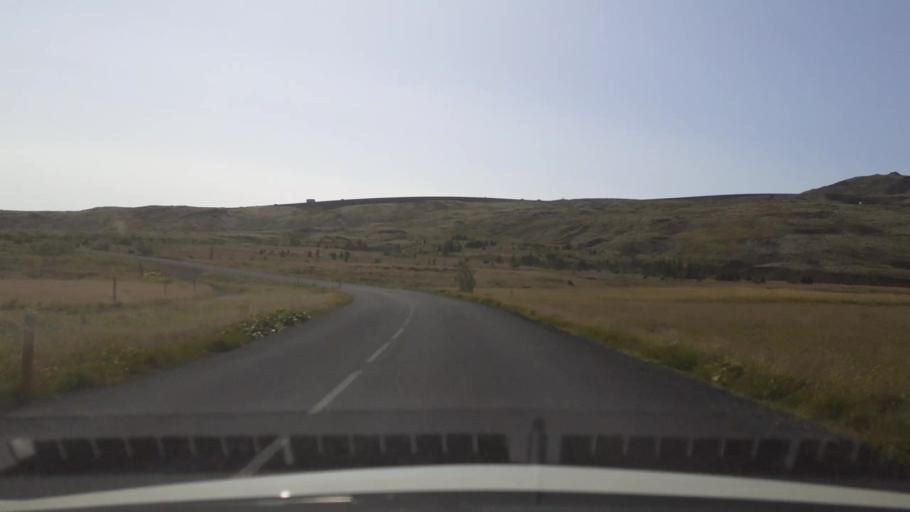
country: IS
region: South
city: Hveragerdi
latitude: 64.0177
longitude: -21.2090
